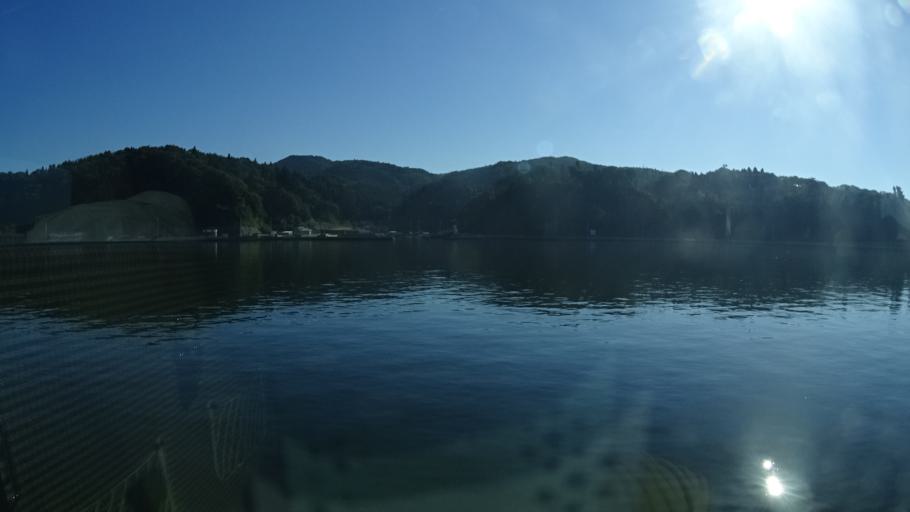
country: JP
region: Iwate
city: Ofunato
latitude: 38.8907
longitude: 141.5940
